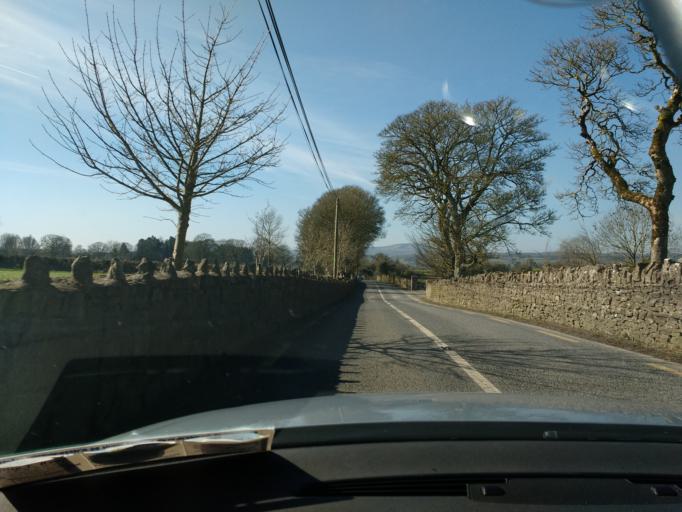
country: IE
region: Munster
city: Thurles
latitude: 52.6898
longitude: -7.9002
